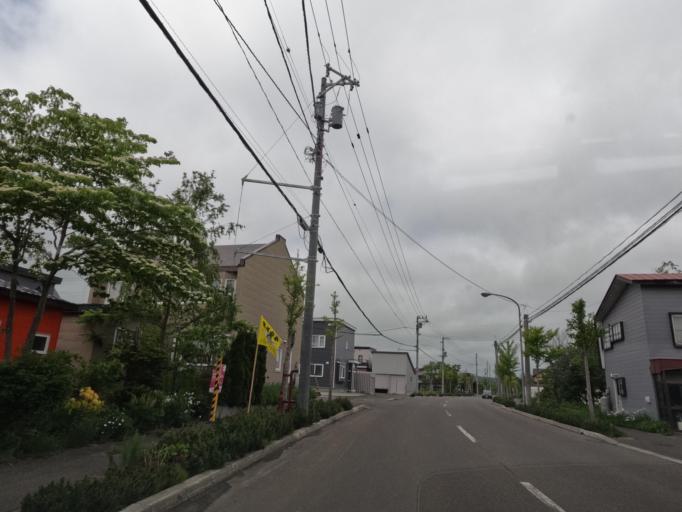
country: JP
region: Hokkaido
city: Tobetsu
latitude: 43.2319
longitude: 141.5156
